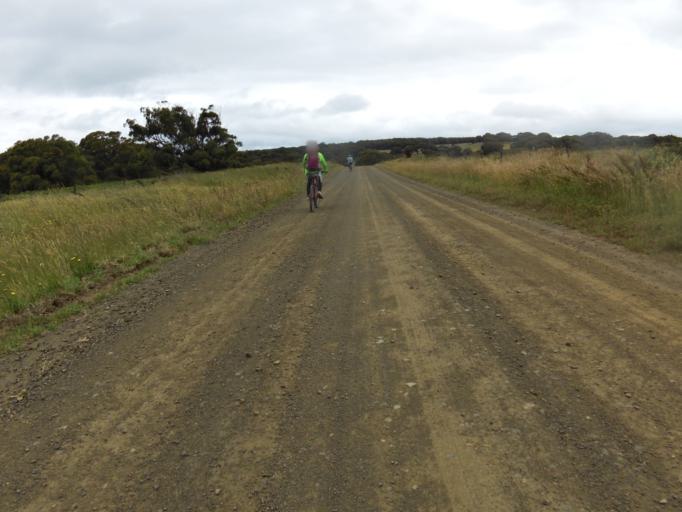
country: AU
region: Victoria
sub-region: Bass Coast
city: Cowes
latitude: -38.3837
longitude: 145.3872
